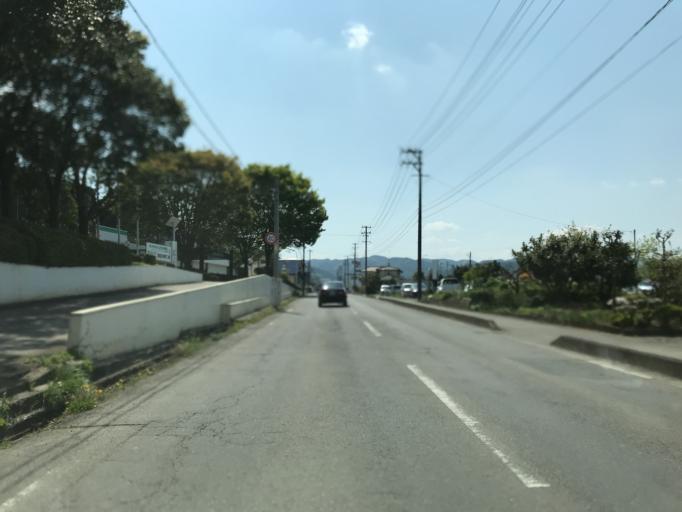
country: JP
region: Ibaraki
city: Kitaibaraki
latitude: 36.8936
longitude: 140.7525
